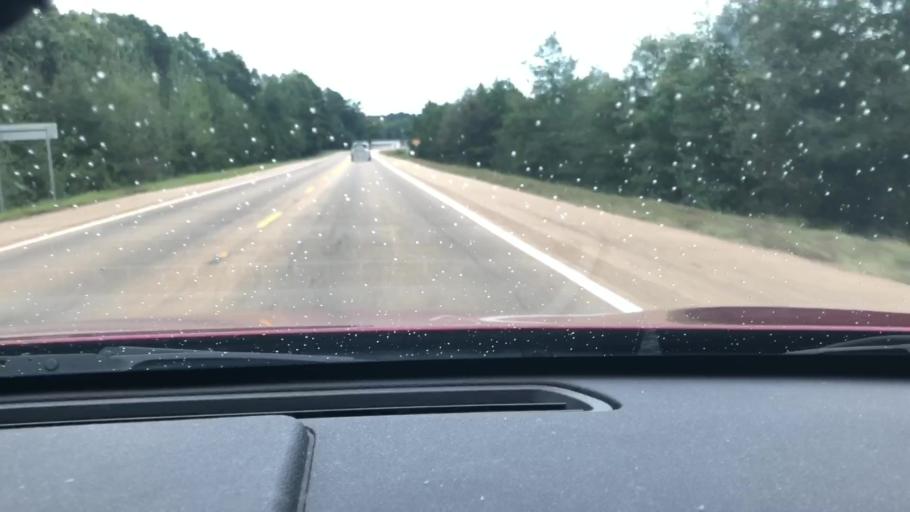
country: US
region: Arkansas
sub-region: Lafayette County
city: Stamps
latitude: 33.3672
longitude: -93.5194
